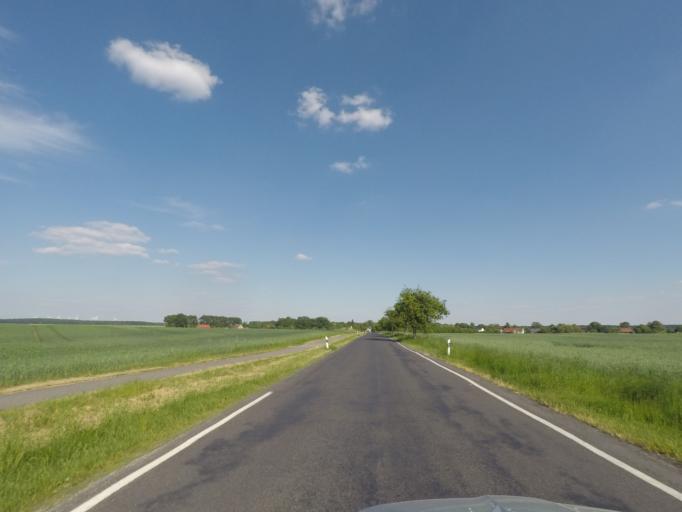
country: DE
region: Brandenburg
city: Werftpfuhl
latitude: 52.7324
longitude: 13.8614
